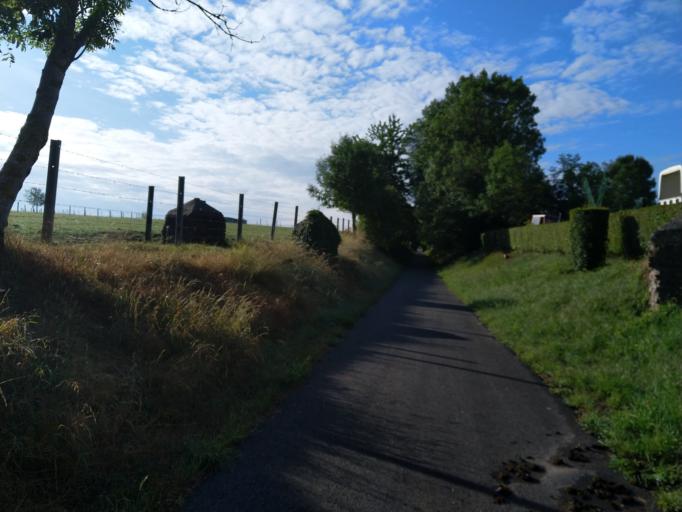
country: BE
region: Wallonia
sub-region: Province du Hainaut
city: Binche
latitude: 50.4329
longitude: 4.1528
